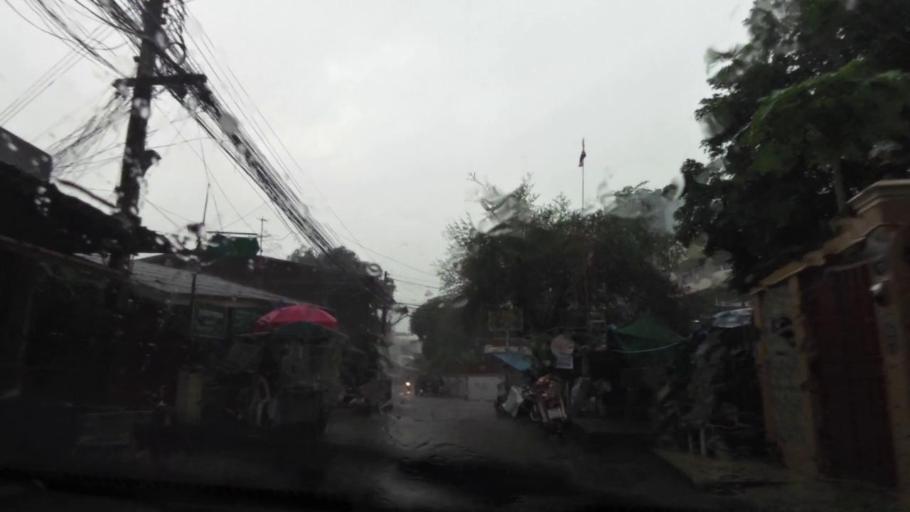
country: TH
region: Bangkok
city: Phra Khanong
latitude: 13.7158
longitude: 100.5977
